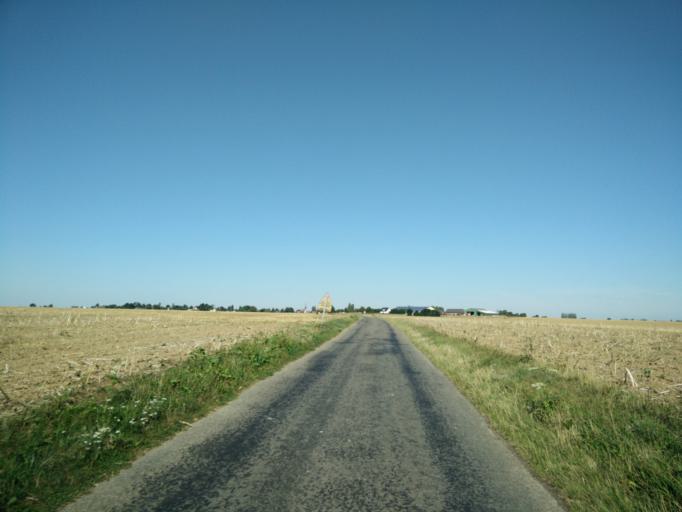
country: FR
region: Haute-Normandie
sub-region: Departement de l'Eure
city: Saint-Pierre-des-Fleurs
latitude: 49.1747
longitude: 0.9960
